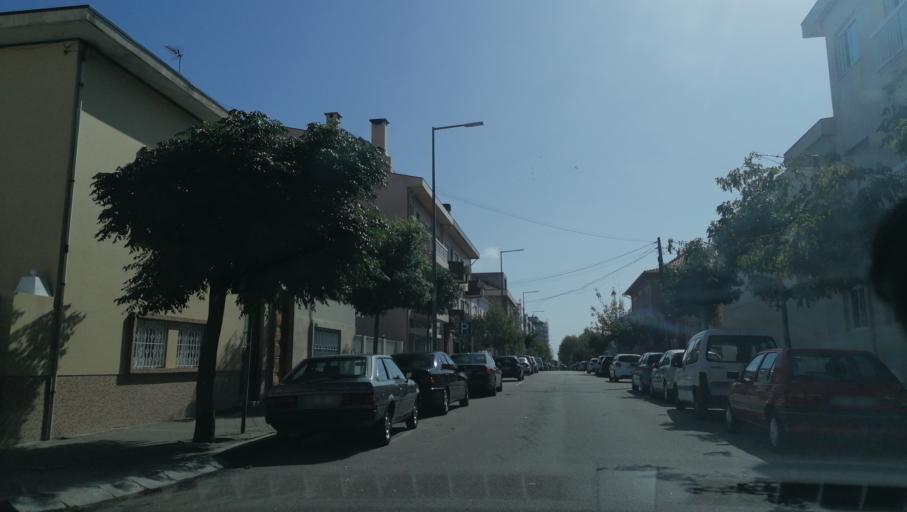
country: PT
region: Aveiro
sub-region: Espinho
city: Espinho
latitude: 41.0112
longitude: -8.6370
